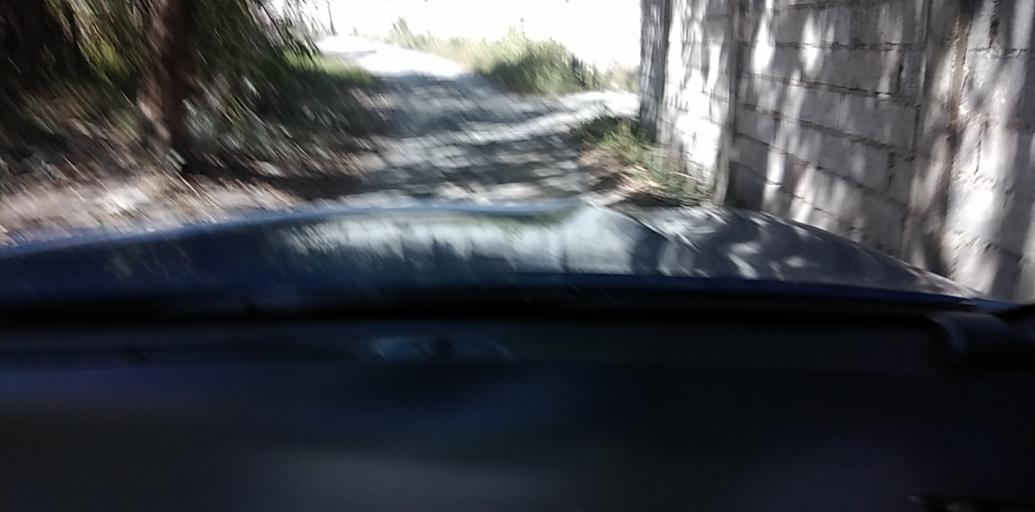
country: PH
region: Central Luzon
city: Santol
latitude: 15.1669
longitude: 120.4882
